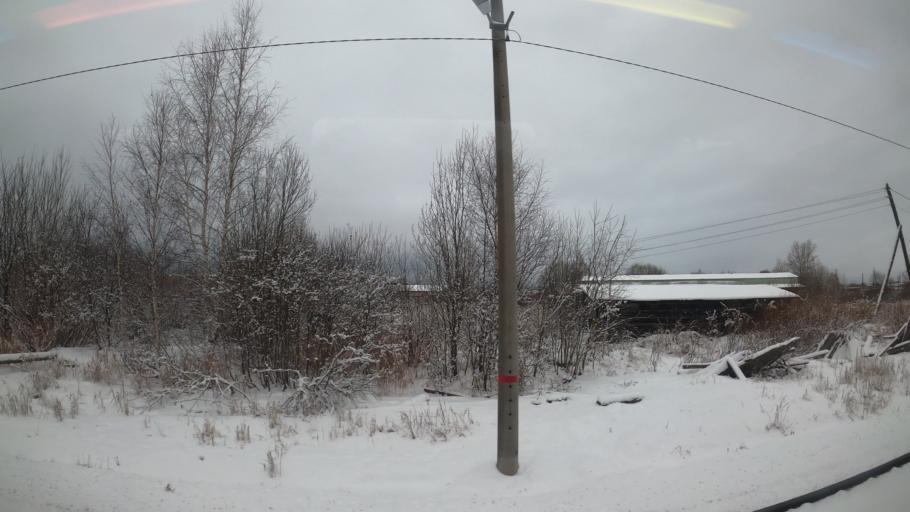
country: RU
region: Jaroslavl
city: Pereslavl'-Zalesskiy
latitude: 56.7340
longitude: 38.8942
